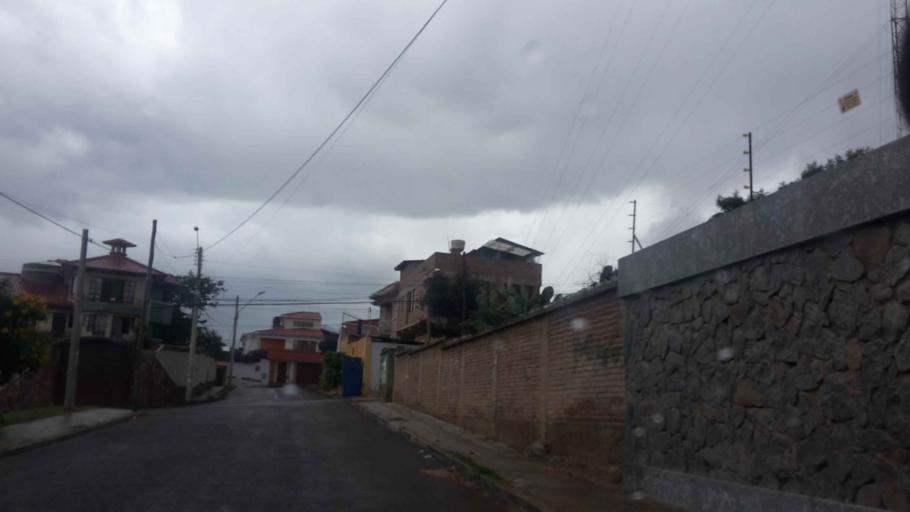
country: BO
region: Cochabamba
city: Cochabamba
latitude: -17.3573
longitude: -66.1576
